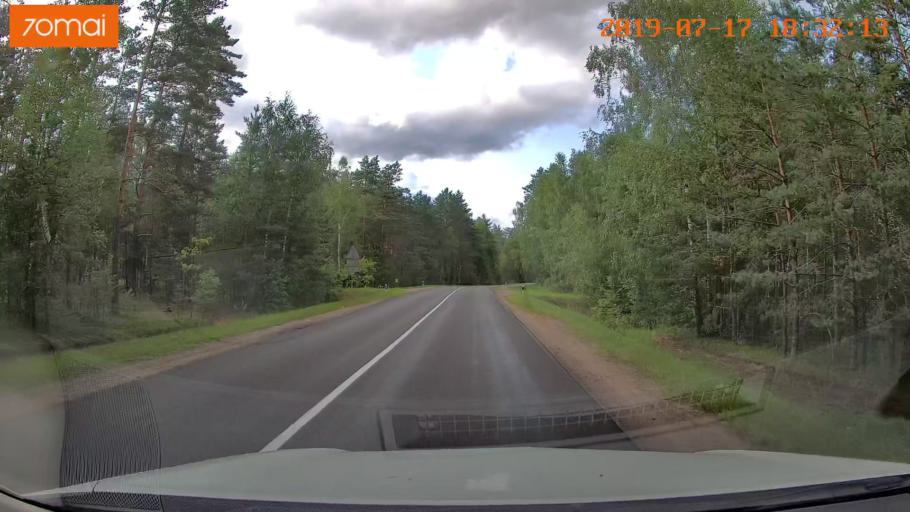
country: BY
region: Mogilev
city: Asipovichy
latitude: 53.2682
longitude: 28.6766
